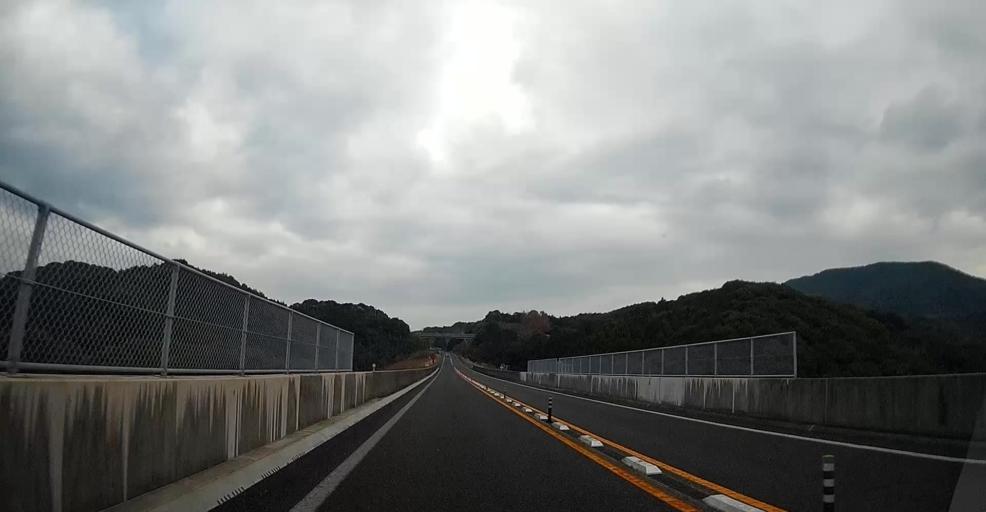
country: JP
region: Kumamoto
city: Hondo
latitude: 32.5080
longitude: 130.3416
